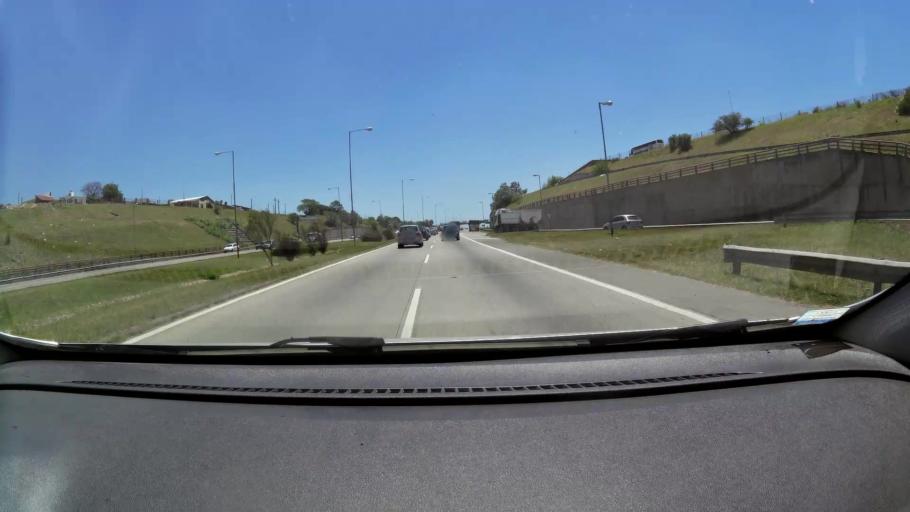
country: AR
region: Cordoba
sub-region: Departamento de Capital
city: Cordoba
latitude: -31.3949
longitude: -64.1275
